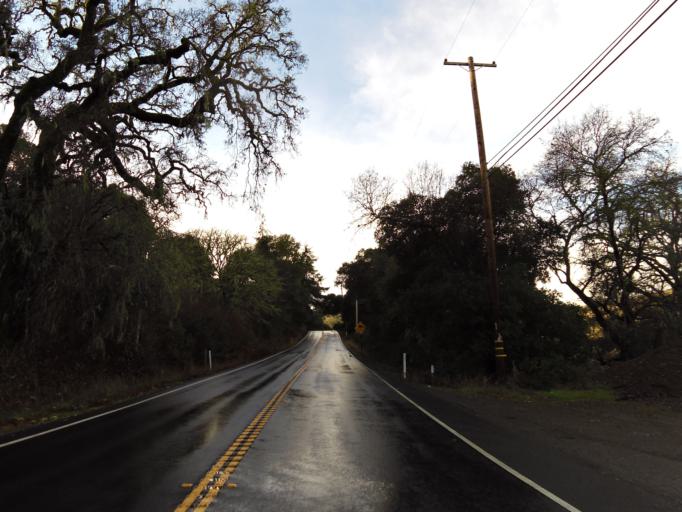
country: US
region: California
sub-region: Sonoma County
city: Cloverdale
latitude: 38.8757
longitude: -123.1056
